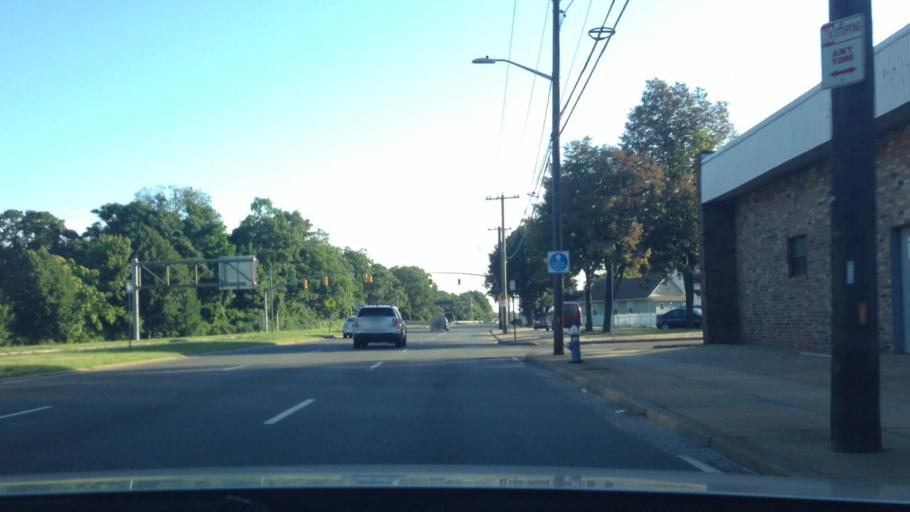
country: US
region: New York
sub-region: Nassau County
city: Hempstead
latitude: 40.6937
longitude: -73.6316
